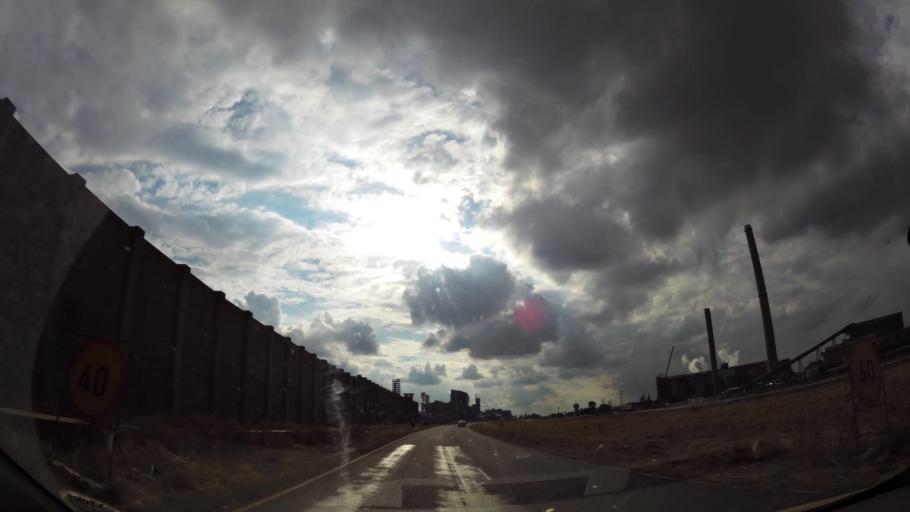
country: ZA
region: Orange Free State
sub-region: Fezile Dabi District Municipality
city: Sasolburg
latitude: -26.8259
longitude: 27.8482
